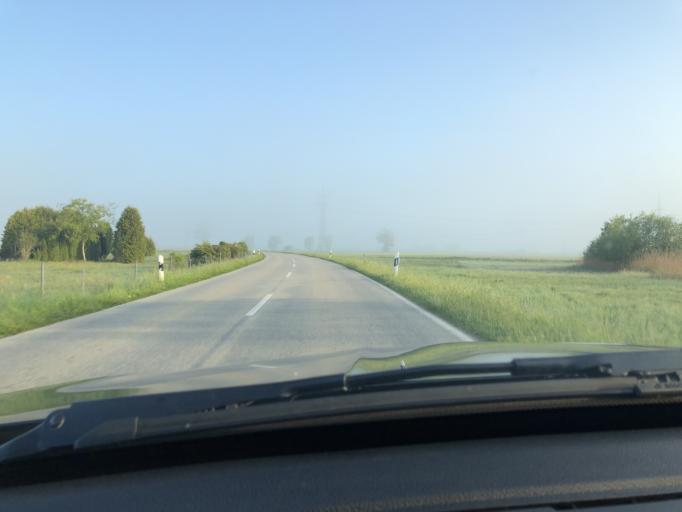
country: DE
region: Bavaria
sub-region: Upper Bavaria
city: Wolfersdorf
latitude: 48.4429
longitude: 11.7216
